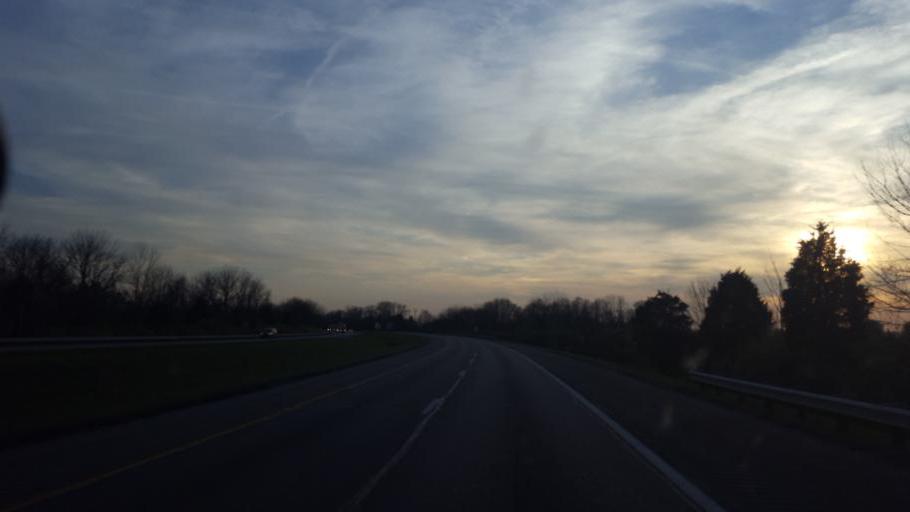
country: US
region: Ohio
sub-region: Warren County
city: Lebanon
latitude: 39.4121
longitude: -84.1642
